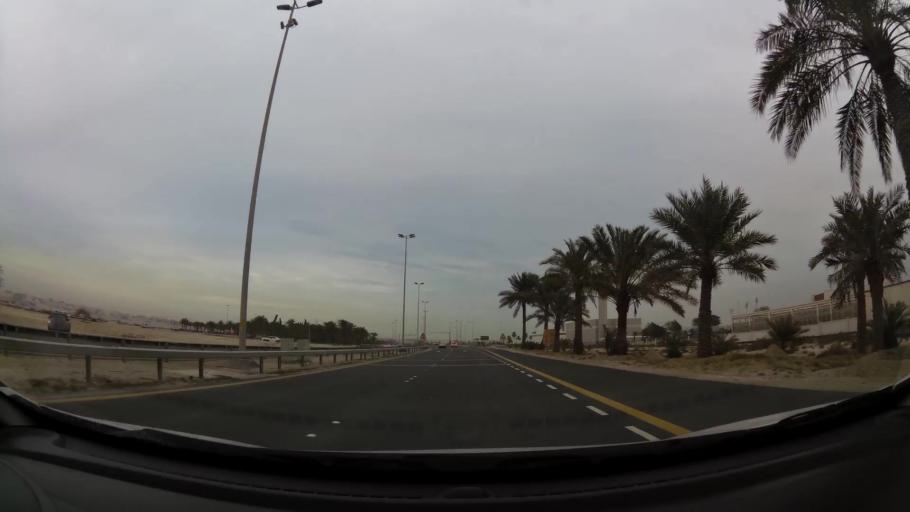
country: BH
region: Northern
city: Ar Rifa'
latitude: 26.1027
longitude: 50.5624
